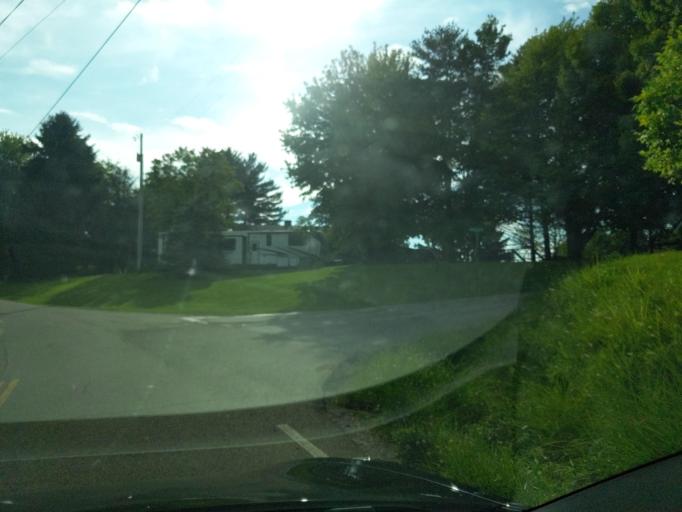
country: US
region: Ohio
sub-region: Fairfield County
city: Lancaster
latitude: 39.5636
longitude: -82.6036
